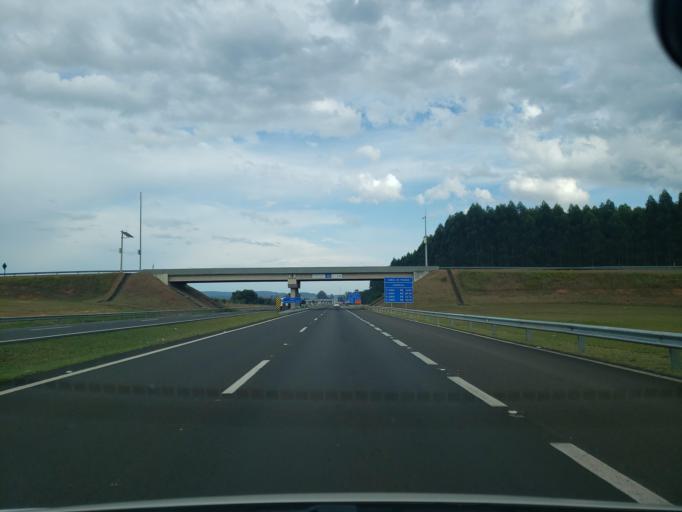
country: BR
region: Sao Paulo
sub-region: Itirapina
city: Itirapina
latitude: -22.2623
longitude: -47.8935
